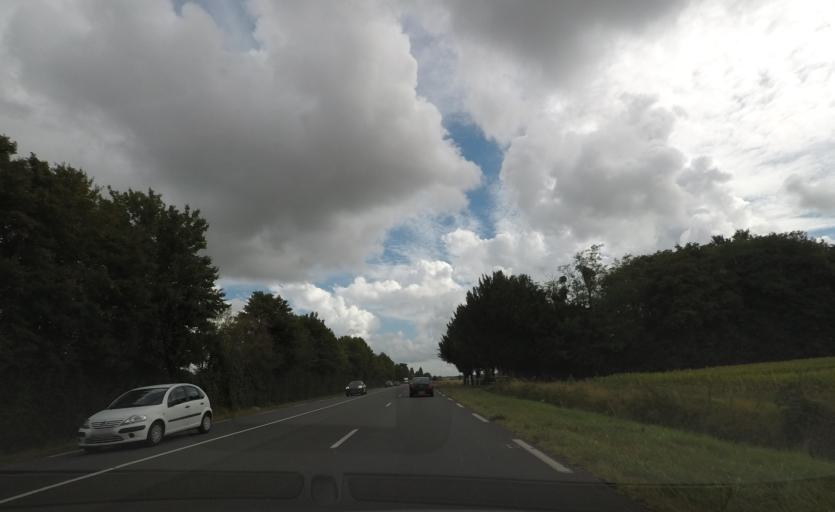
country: FR
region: Pays de la Loire
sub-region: Departement de Maine-et-Loire
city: Pellouailles-les-Vignes
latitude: 47.5310
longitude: -0.4188
